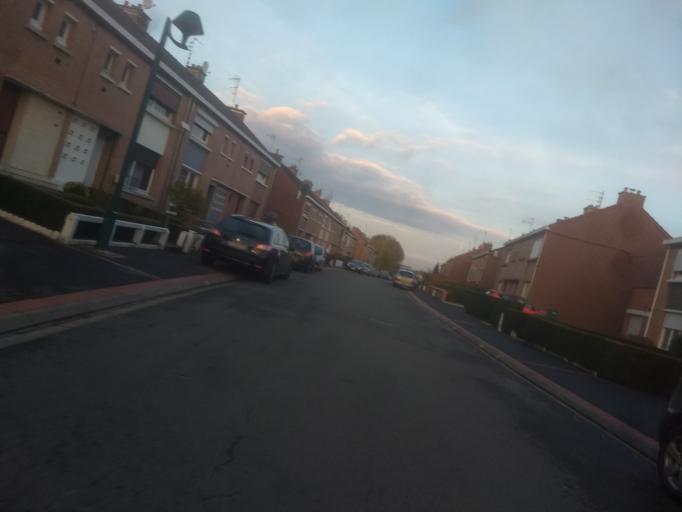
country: FR
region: Nord-Pas-de-Calais
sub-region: Departement du Pas-de-Calais
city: Dainville
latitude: 50.2849
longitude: 2.7348
